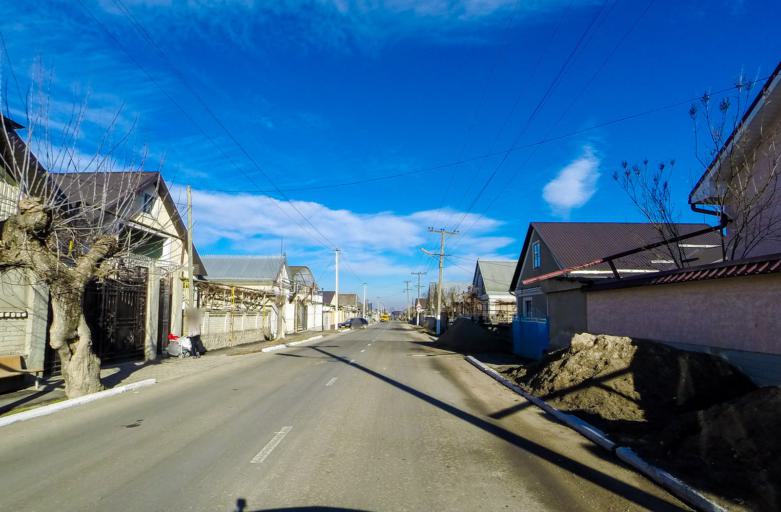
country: RU
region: Kabardino-Balkariya
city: Belaya Rechka
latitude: 43.4307
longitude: 43.5787
